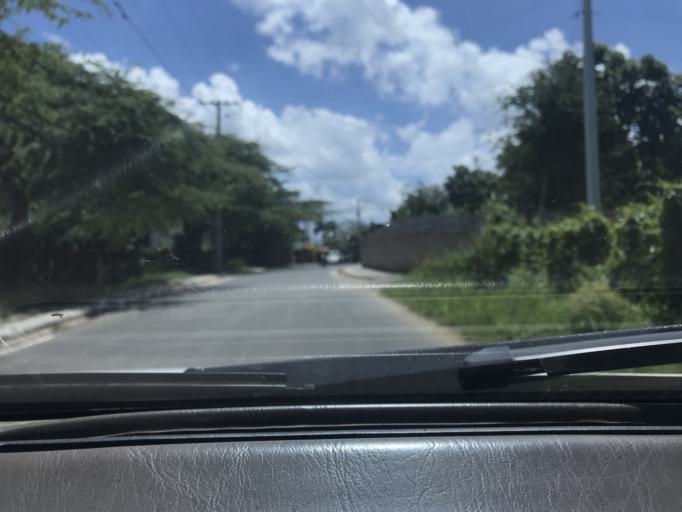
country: DO
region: Santiago
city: Santiago de los Caballeros
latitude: 19.4207
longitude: -70.7080
